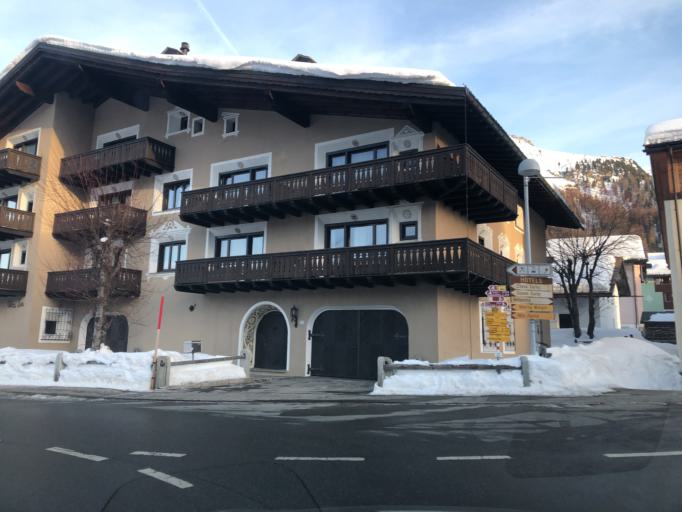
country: CH
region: Grisons
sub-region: Maloja District
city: Silvaplana
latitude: 46.4588
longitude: 9.8100
